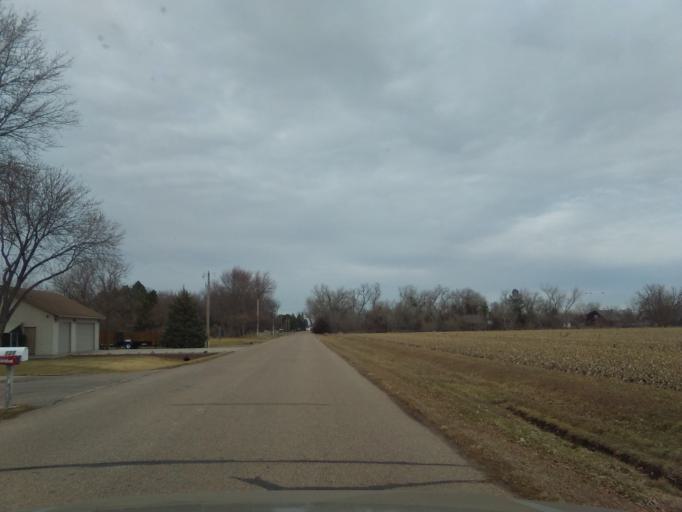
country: US
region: Nebraska
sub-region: Hall County
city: Grand Island
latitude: 40.7726
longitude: -98.4118
